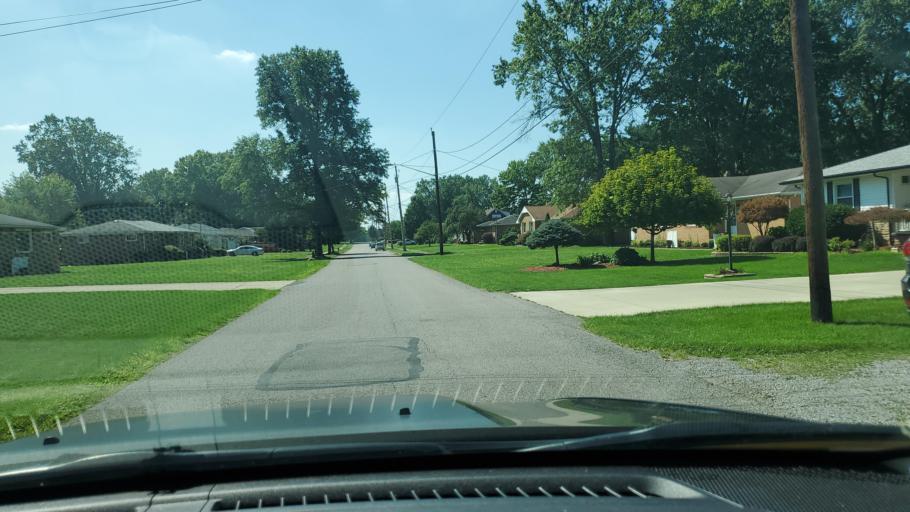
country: US
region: Ohio
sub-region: Trumbull County
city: Girard
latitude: 41.1699
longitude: -80.6869
